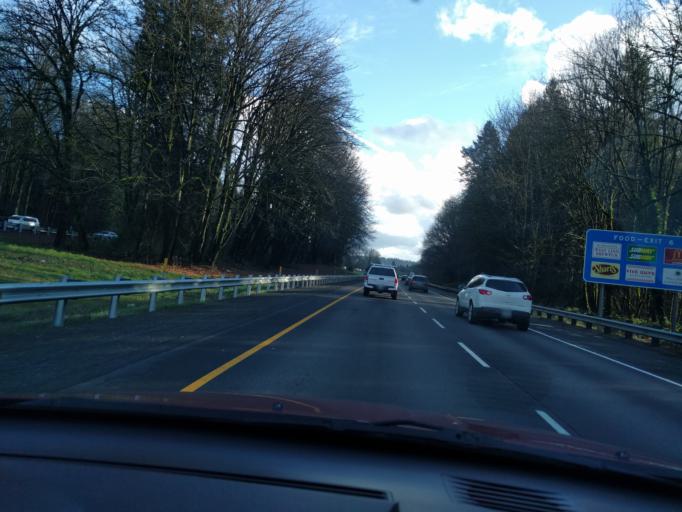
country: US
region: Oregon
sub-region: Clackamas County
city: West Linn
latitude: 45.3585
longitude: -122.6670
